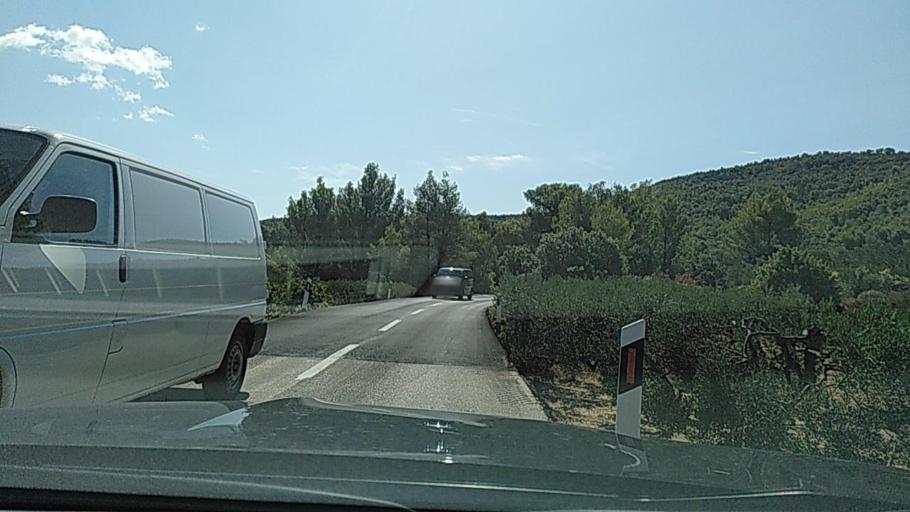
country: HR
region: Splitsko-Dalmatinska
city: Jelsa
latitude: 43.1467
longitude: 16.8009
